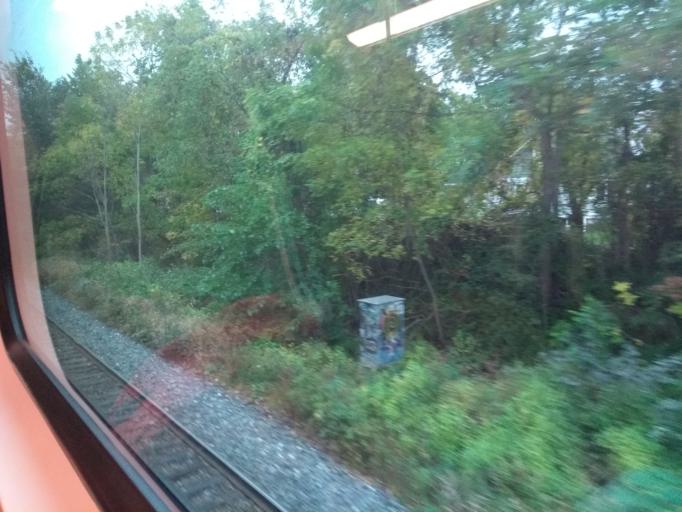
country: CA
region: Ontario
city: Oakville
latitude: 43.1975
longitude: -79.5652
